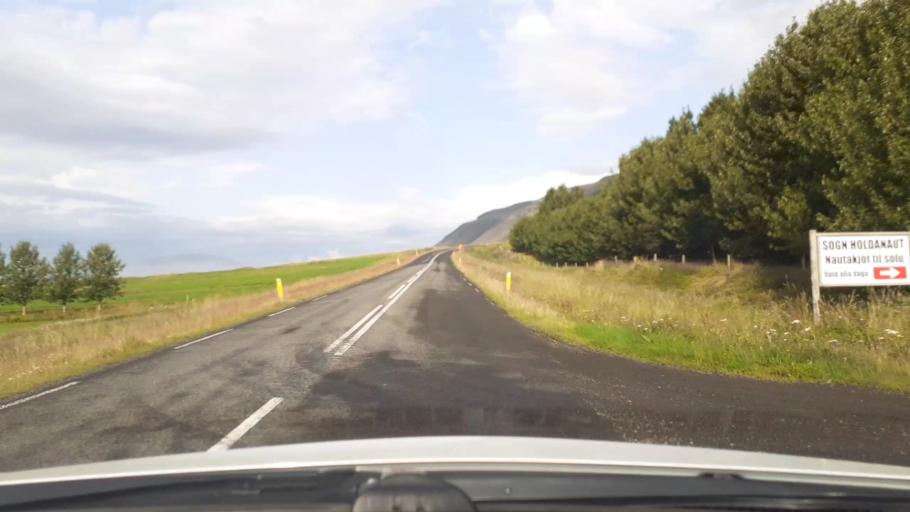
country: IS
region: Capital Region
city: Mosfellsbaer
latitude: 64.3409
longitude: -21.5515
